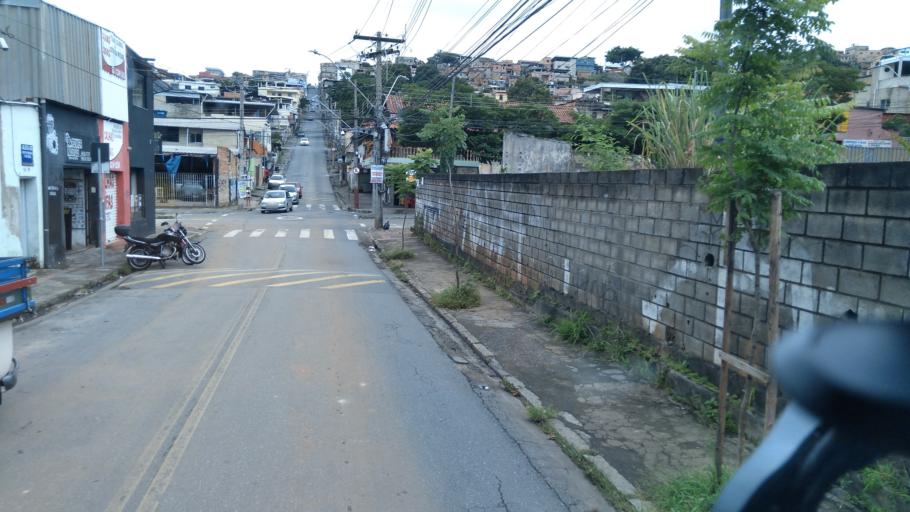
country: BR
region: Minas Gerais
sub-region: Belo Horizonte
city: Belo Horizonte
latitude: -19.9103
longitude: -43.8946
